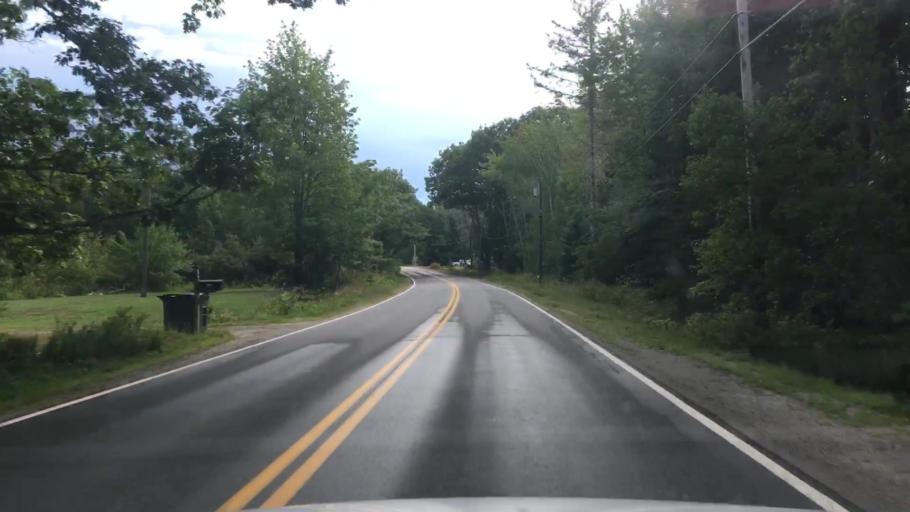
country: US
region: Maine
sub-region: Hancock County
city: Trenton
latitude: 44.4657
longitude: -68.4238
